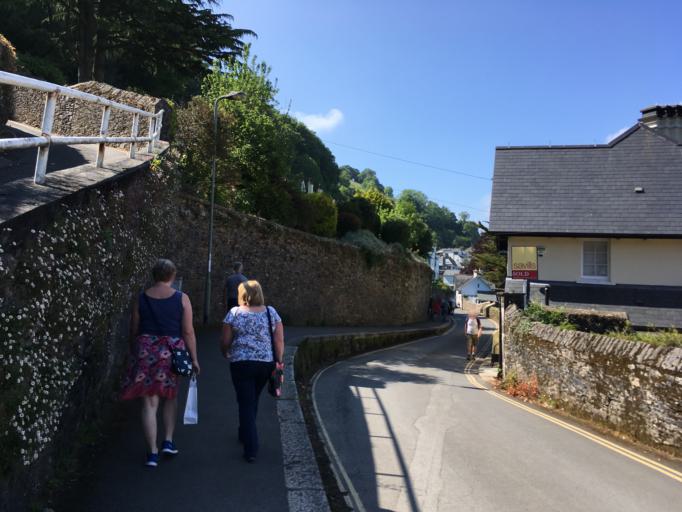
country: GB
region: England
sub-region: Devon
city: Dartmouth
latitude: 50.3446
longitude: -3.5759
